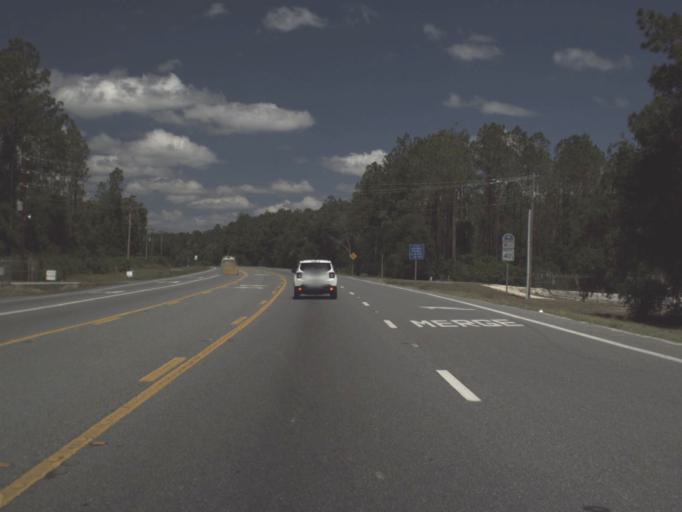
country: US
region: Florida
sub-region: Marion County
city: Silver Springs Shores
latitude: 29.1836
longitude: -81.8911
